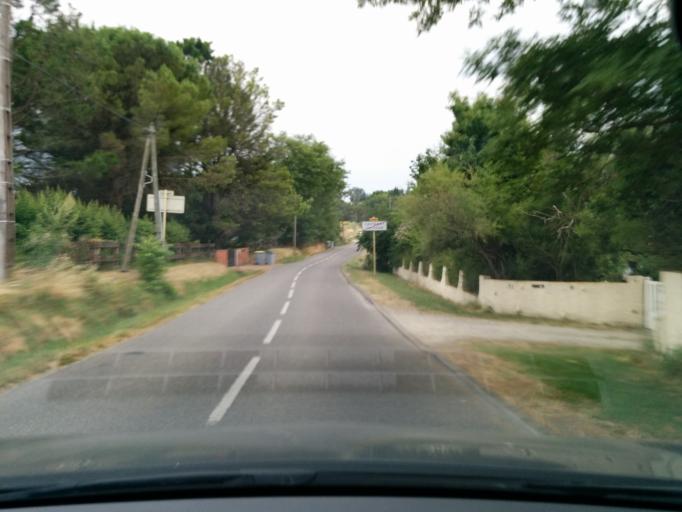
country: FR
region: Midi-Pyrenees
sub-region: Departement de la Haute-Garonne
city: Castanet-Tolosan
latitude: 43.5076
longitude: 1.4876
